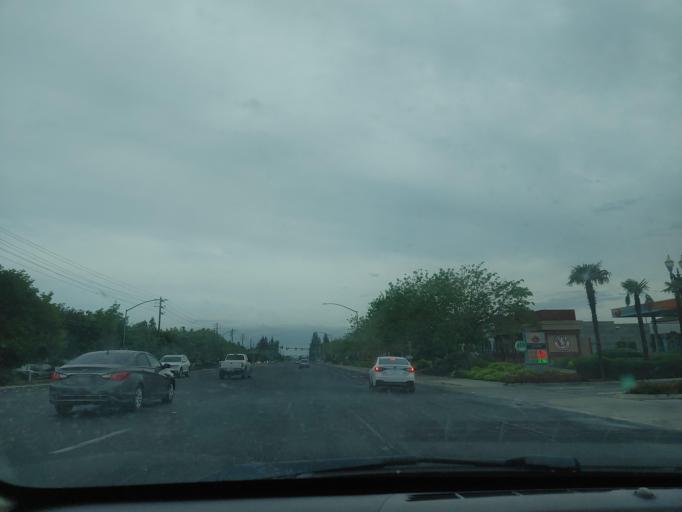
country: US
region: California
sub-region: Stanislaus County
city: Salida
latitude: 37.6981
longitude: -121.0499
